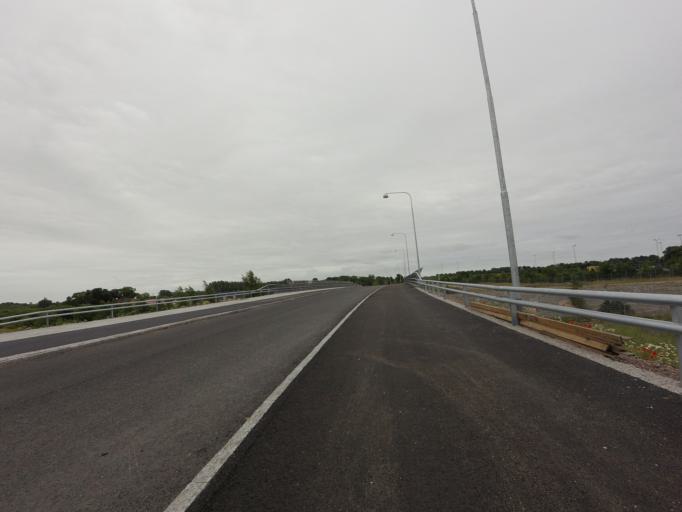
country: SE
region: Skane
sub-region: Malmo
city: Bunkeflostrand
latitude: 55.5598
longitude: 12.9452
